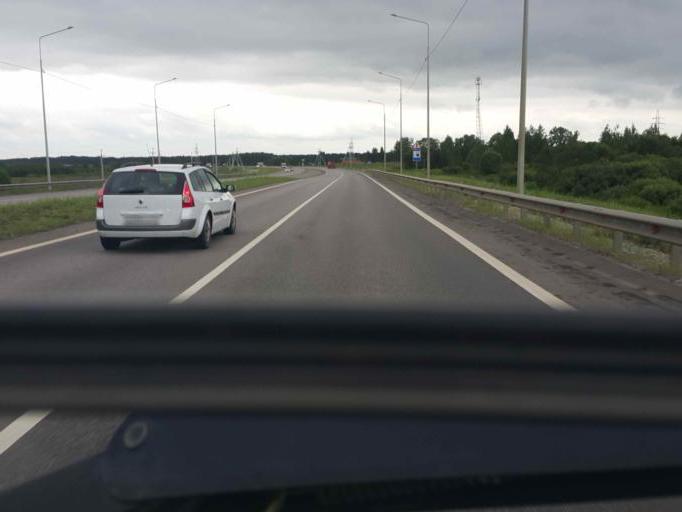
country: RU
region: Tambov
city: Zavoronezhskoye
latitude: 52.8691
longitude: 40.7592
